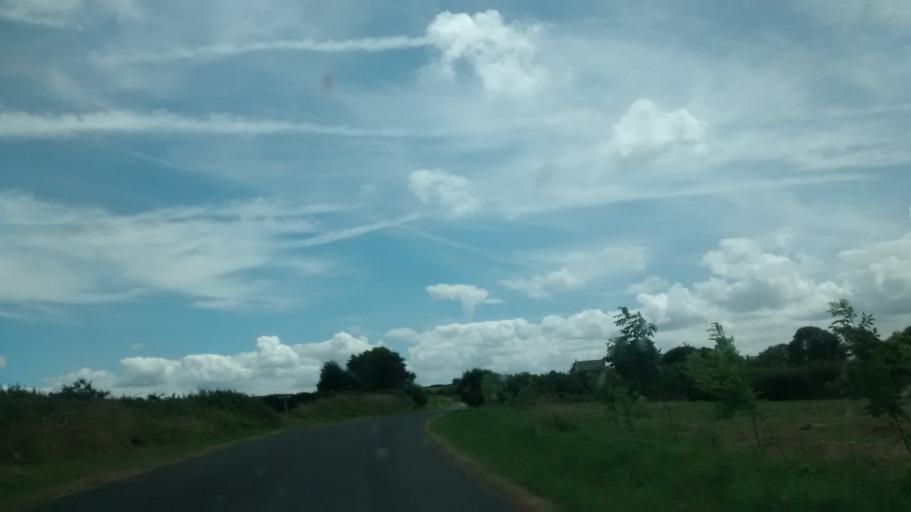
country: FR
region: Brittany
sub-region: Departement du Finistere
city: Plouguerneau
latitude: 48.6213
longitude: -4.4704
